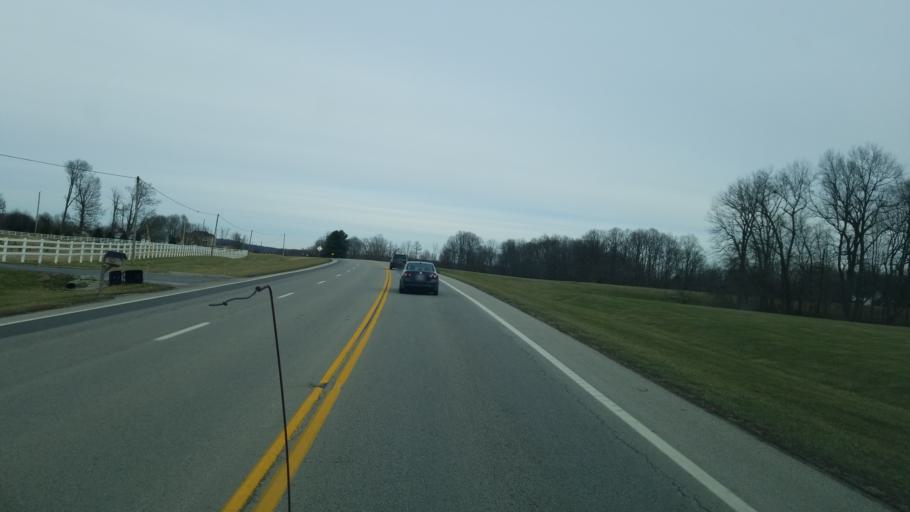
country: US
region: Ohio
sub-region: Highland County
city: Hillsboro
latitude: 39.1639
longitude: -83.6346
